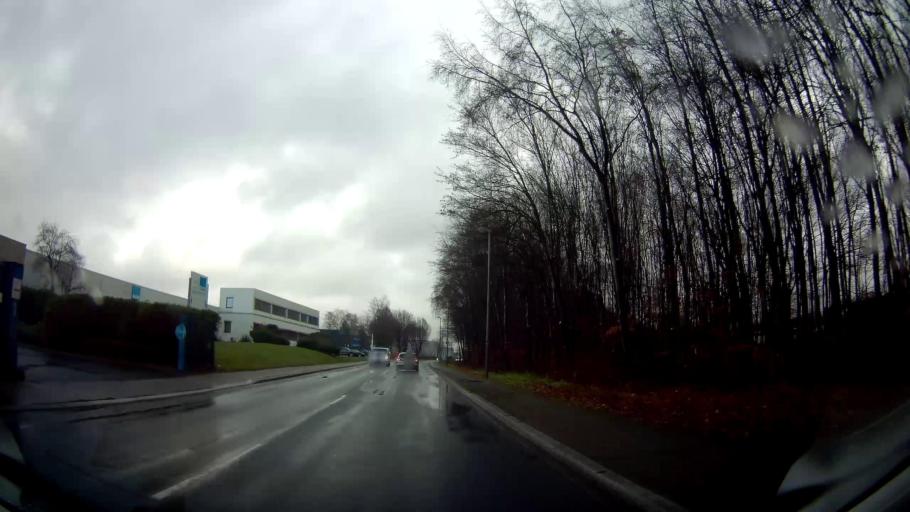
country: DE
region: North Rhine-Westphalia
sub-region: Regierungsbezirk Arnsberg
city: Herne
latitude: 51.5099
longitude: 7.2691
